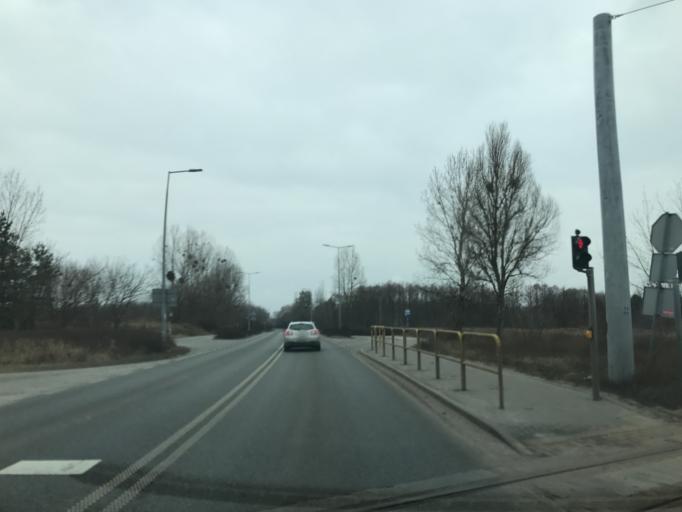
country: PL
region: Kujawsko-Pomorskie
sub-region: Bydgoszcz
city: Fordon
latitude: 53.1044
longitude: 18.1071
